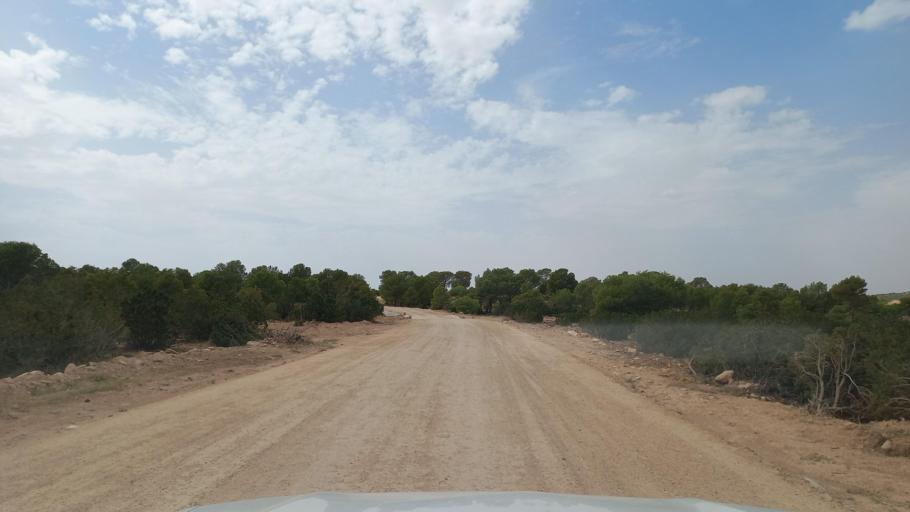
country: TN
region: Al Qasrayn
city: Kasserine
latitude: 35.3824
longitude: 8.8796
